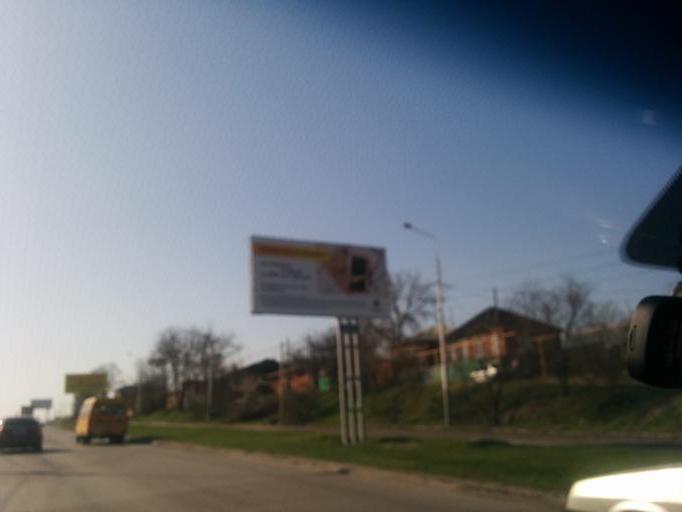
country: RU
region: Rostov
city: Shakhty
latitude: 47.7099
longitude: 40.1758
